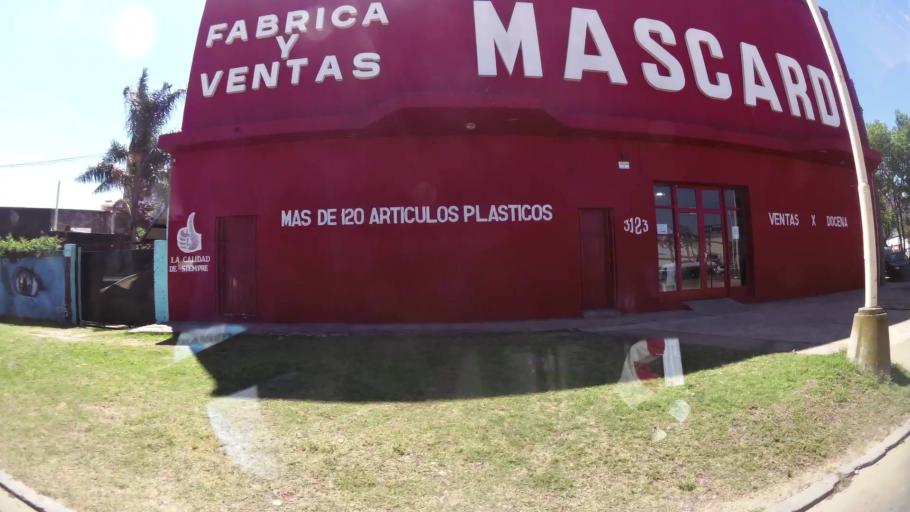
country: AR
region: Santa Fe
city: Santa Fe de la Vera Cruz
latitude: -31.6429
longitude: -60.6871
